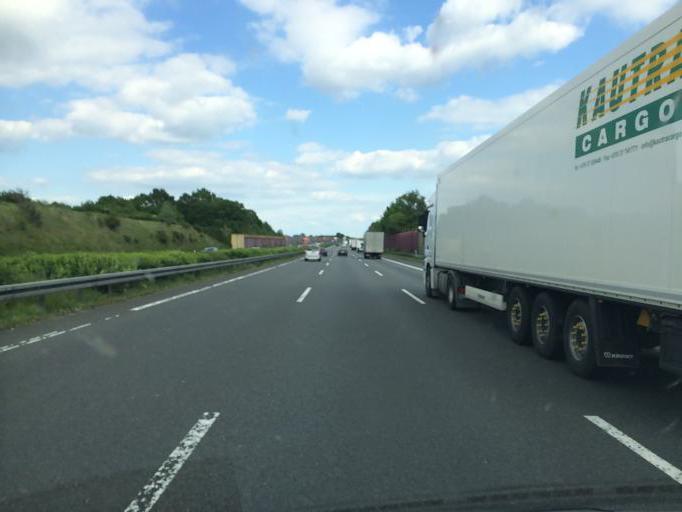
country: DE
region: Lower Saxony
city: Dollbergen
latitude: 52.3591
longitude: 10.1692
